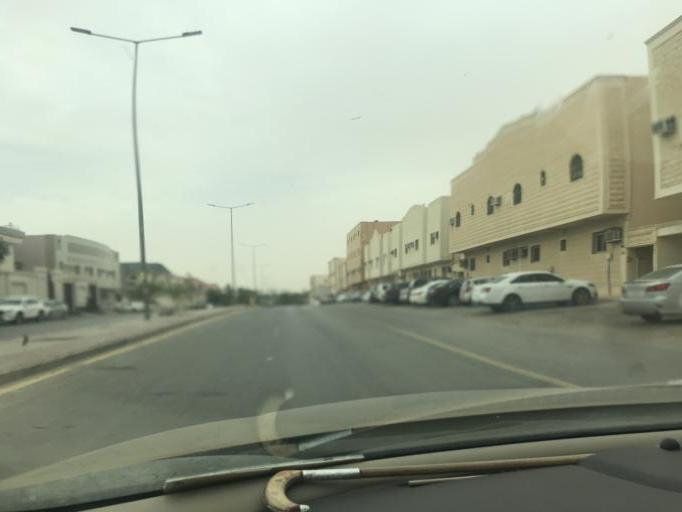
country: SA
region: Ar Riyad
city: Riyadh
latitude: 24.7358
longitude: 46.7576
